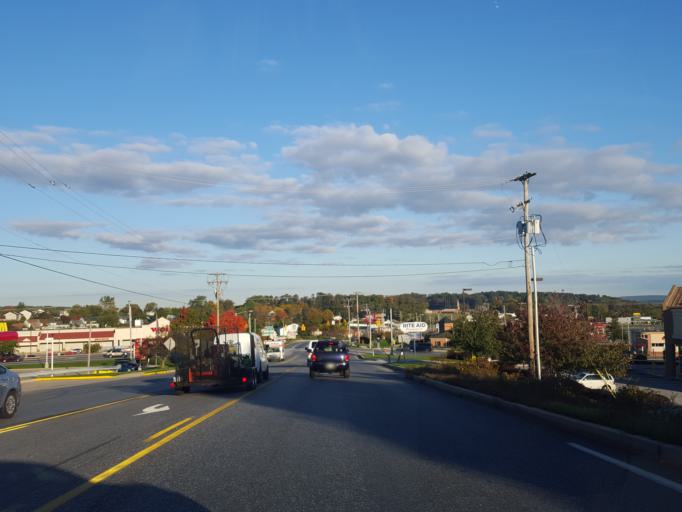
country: US
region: Pennsylvania
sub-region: York County
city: Yoe
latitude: 39.9150
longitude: -76.6283
